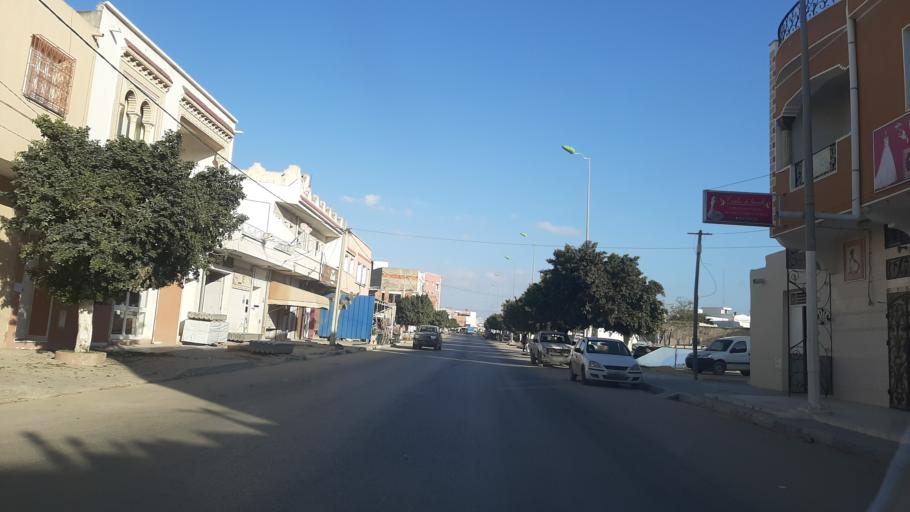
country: TN
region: Al Mahdiyah
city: El Jem
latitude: 35.2975
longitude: 10.7093
